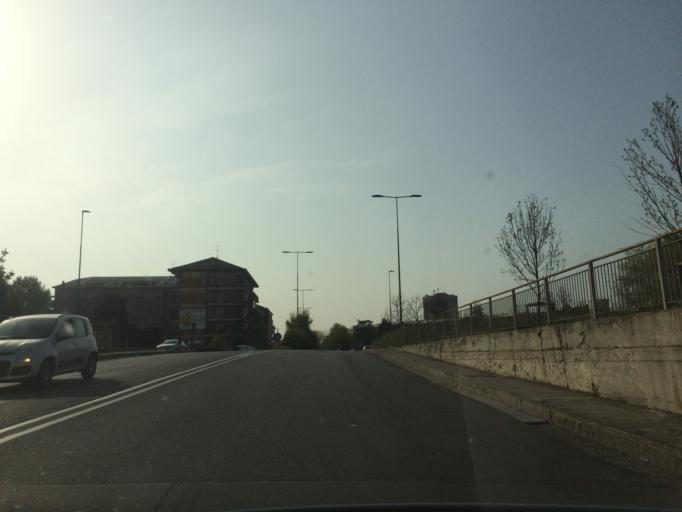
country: IT
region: Lombardy
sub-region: Provincia di Brescia
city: Brescia
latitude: 45.5193
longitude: 10.2195
